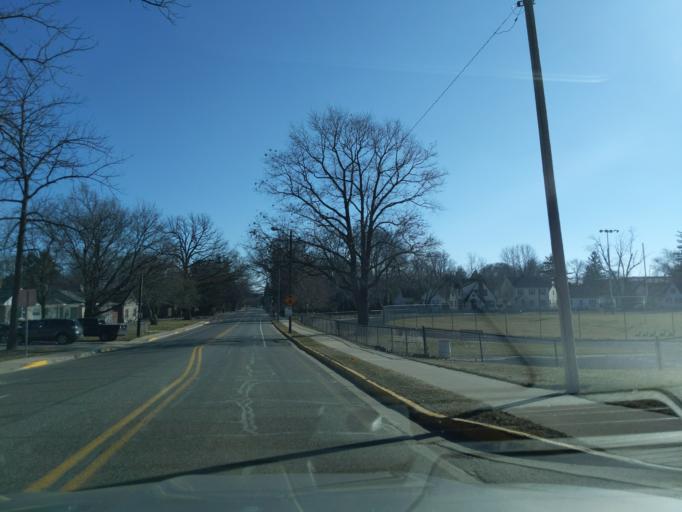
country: US
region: Indiana
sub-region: Tippecanoe County
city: West Lafayette
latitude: 40.4352
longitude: -86.9106
